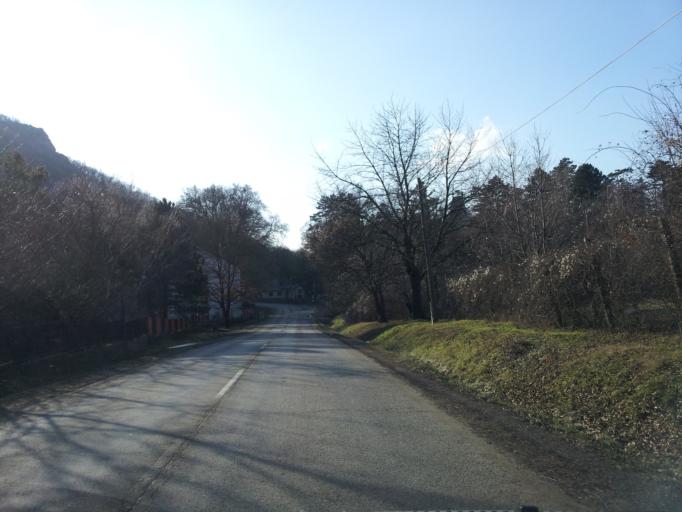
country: HU
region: Pest
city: Csobanka
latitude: 47.6550
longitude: 18.9758
